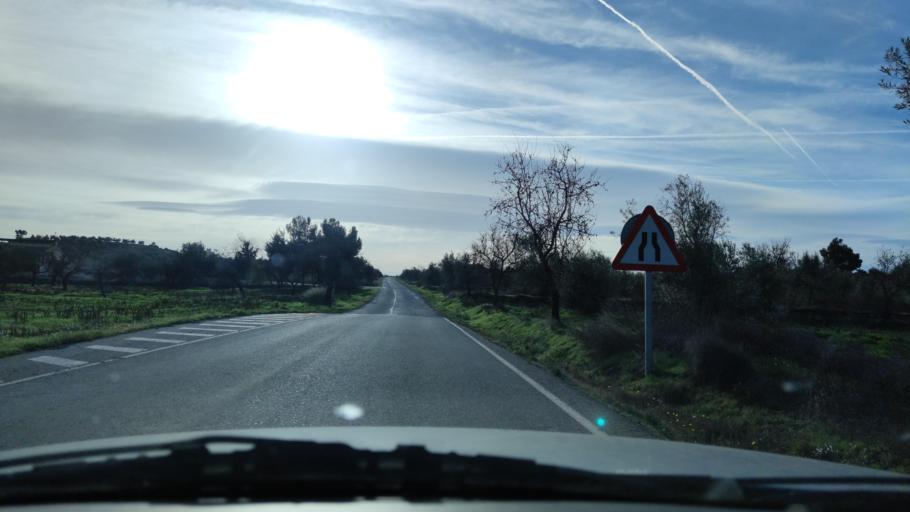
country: ES
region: Catalonia
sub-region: Provincia de Lleida
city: Aspa
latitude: 41.4886
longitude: 0.6747
